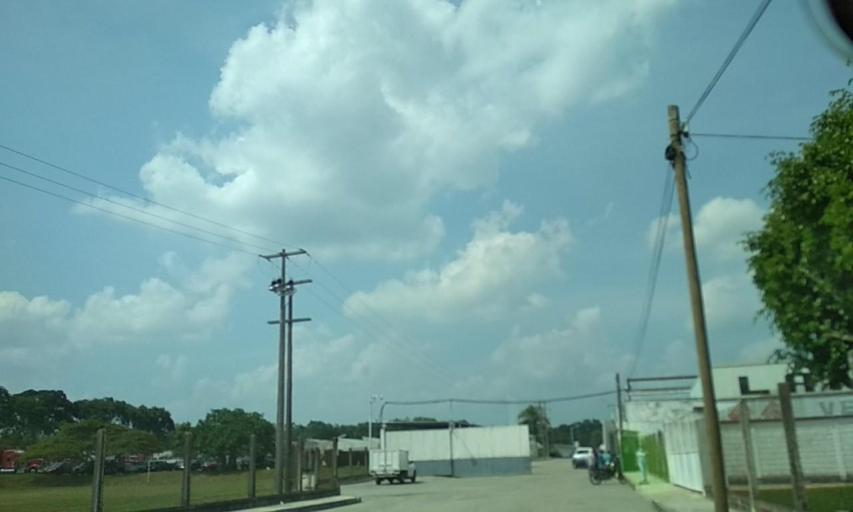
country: MX
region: Veracruz
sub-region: Tlapacoyan
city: San Pedro Tlapacoyan
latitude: 20.0634
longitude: -97.0822
